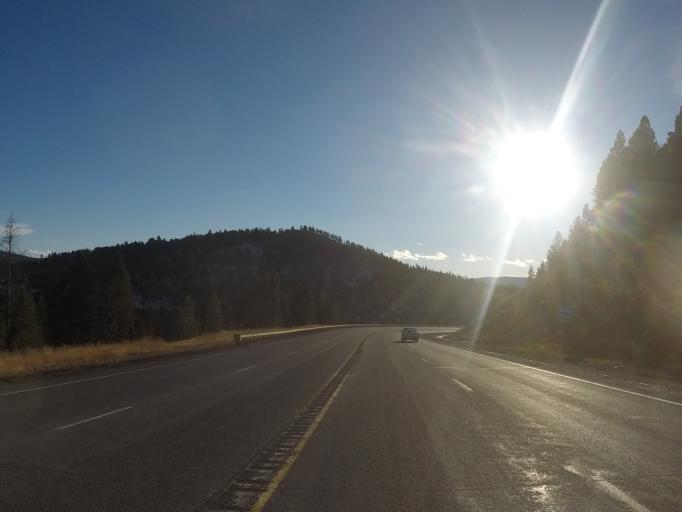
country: US
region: Montana
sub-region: Lewis and Clark County
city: Helena West Side
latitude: 46.5600
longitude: -112.3385
